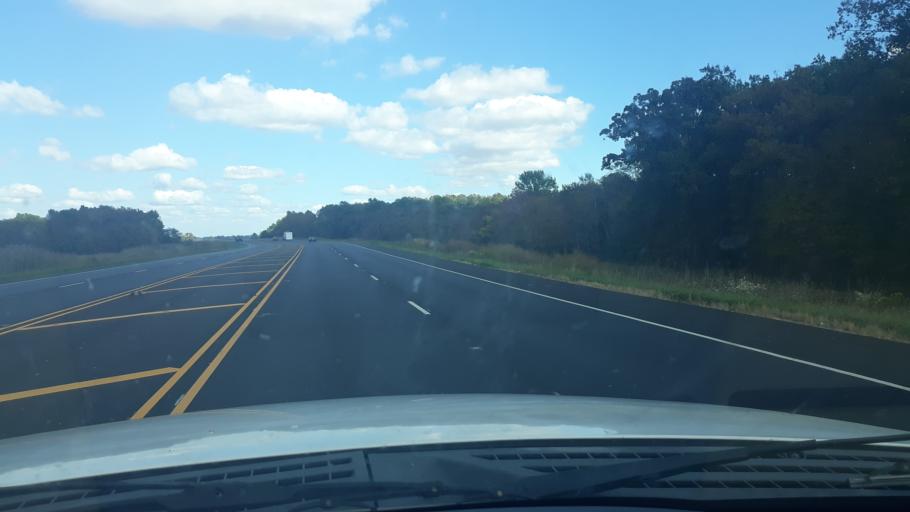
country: US
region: Illinois
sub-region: Saline County
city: Harrisburg
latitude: 37.7477
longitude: -88.5194
